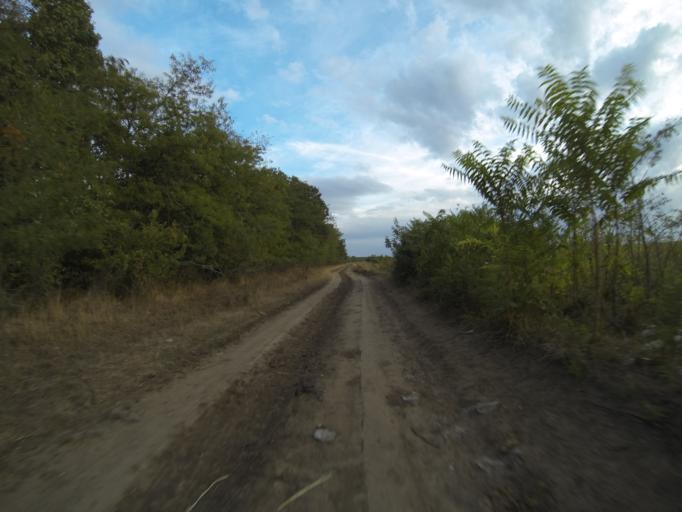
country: RO
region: Dolj
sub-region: Comuna Ceratu
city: Ceratu
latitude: 44.0921
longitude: 23.6728
